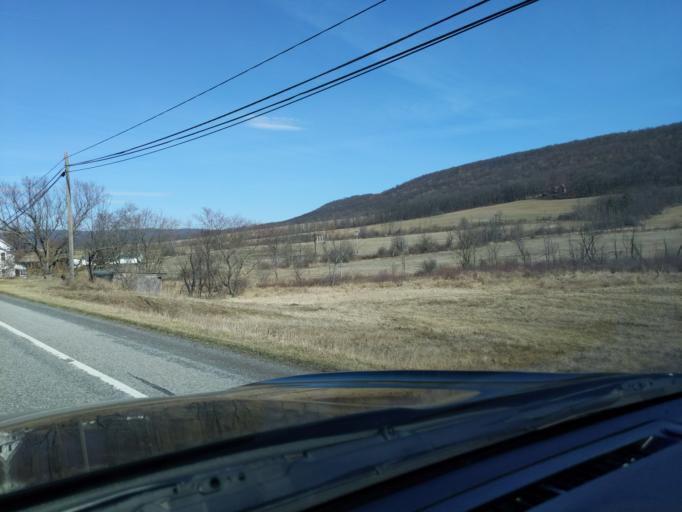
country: US
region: Pennsylvania
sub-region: Blair County
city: Roaring Spring
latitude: 40.3274
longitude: -78.3615
